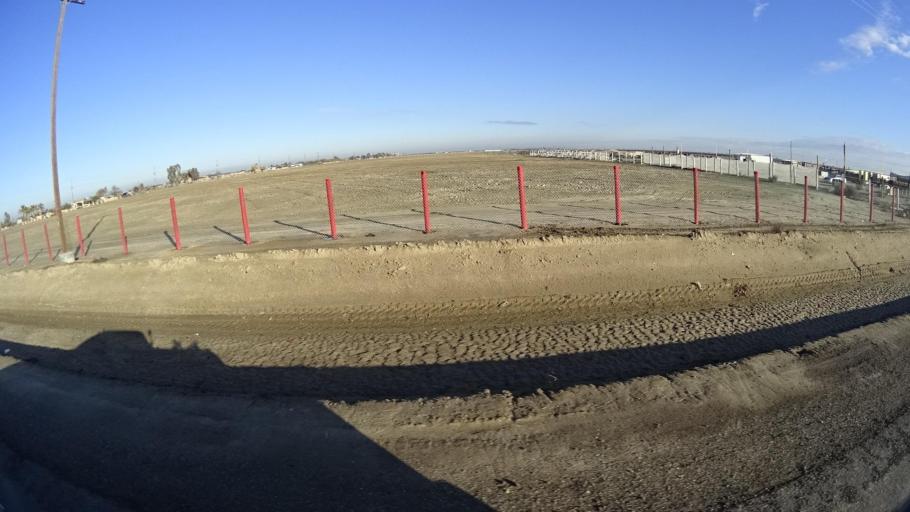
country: US
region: California
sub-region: Kern County
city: Delano
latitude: 35.7759
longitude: -119.2924
